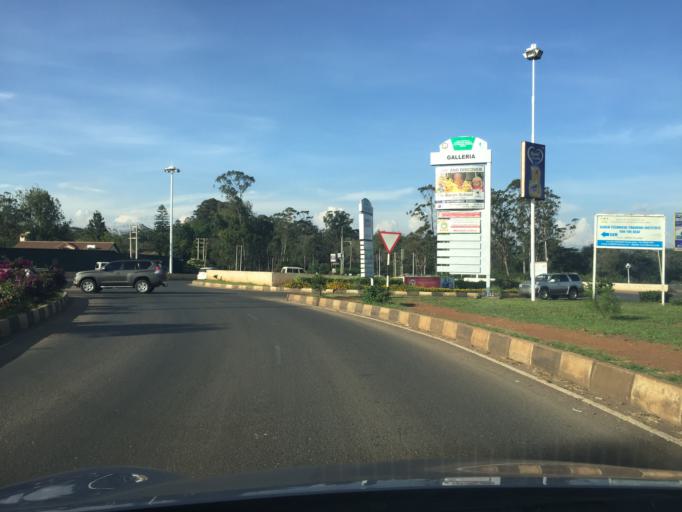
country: KE
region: Nairobi Area
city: Nairobi
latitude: -1.3430
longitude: 36.7665
